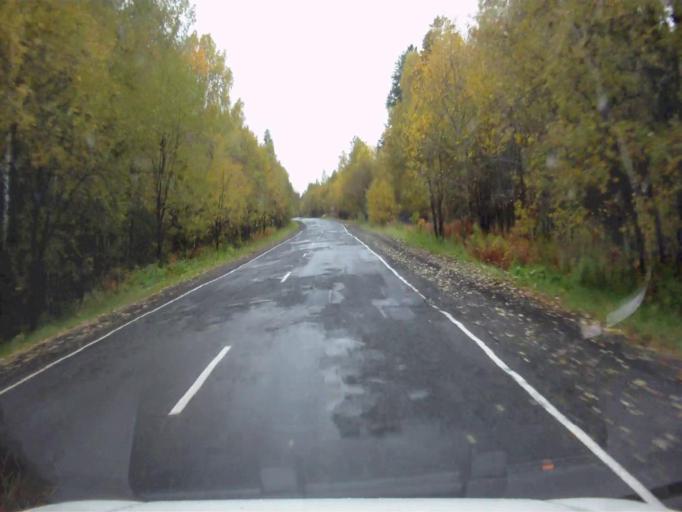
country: RU
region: Chelyabinsk
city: Verkhniy Ufaley
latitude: 56.0456
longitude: 60.1128
